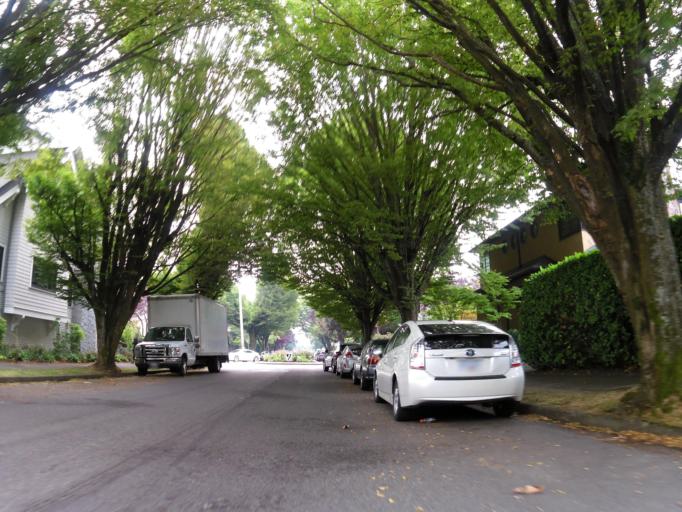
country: CA
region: British Columbia
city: West End
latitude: 49.2749
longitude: -123.1478
